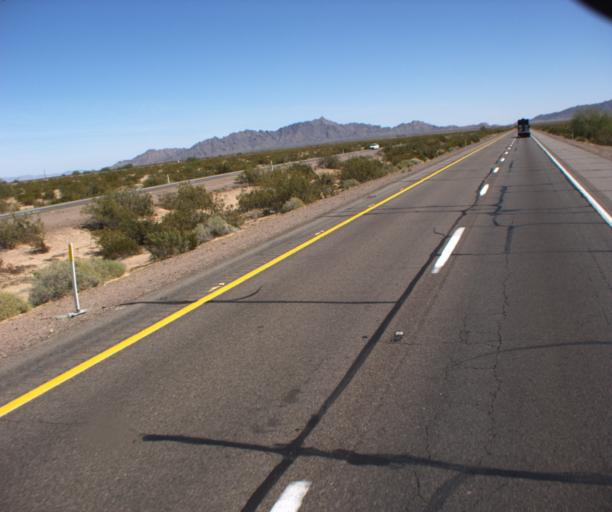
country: US
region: Arizona
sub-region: Yuma County
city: Wellton
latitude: 32.7077
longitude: -113.8590
